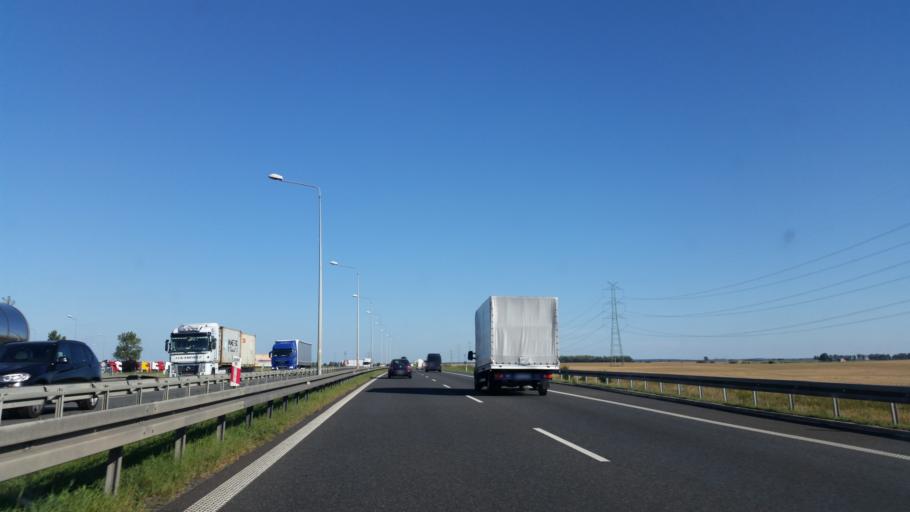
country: PL
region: Opole Voivodeship
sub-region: Powiat brzeski
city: Olszanka
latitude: 50.7572
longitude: 17.4294
